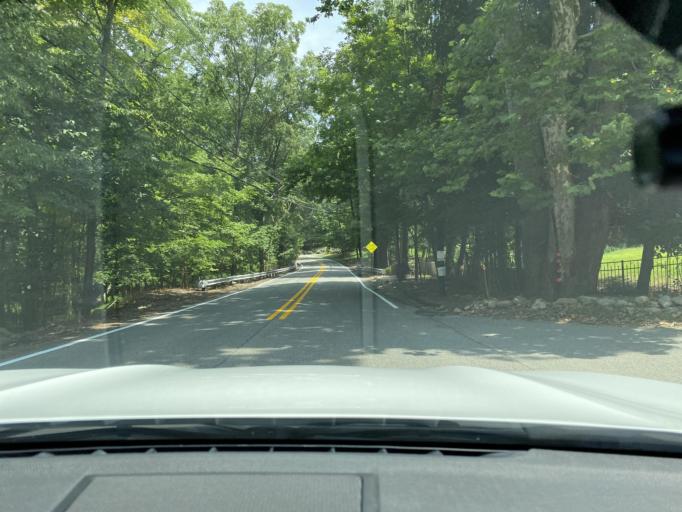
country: US
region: New Jersey
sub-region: Bergen County
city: Mahwah
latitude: 41.0740
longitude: -74.1960
